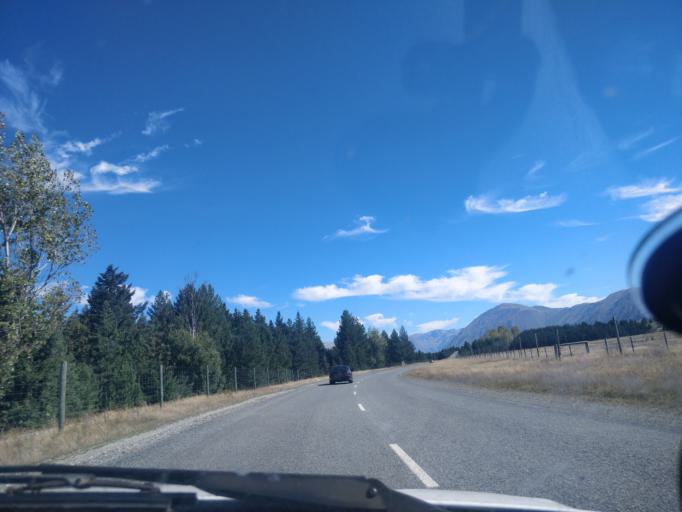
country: NZ
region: Otago
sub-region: Queenstown-Lakes District
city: Wanaka
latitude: -44.2722
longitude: 170.0587
